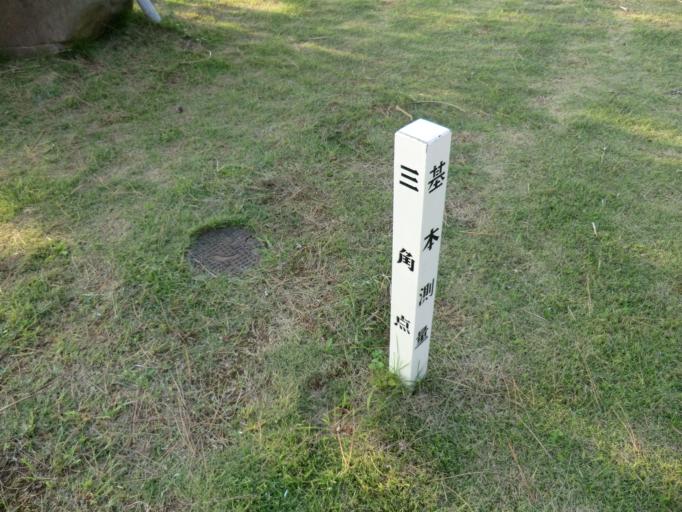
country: JP
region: Niigata
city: Kashiwazaki
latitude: 37.4795
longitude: 138.6180
